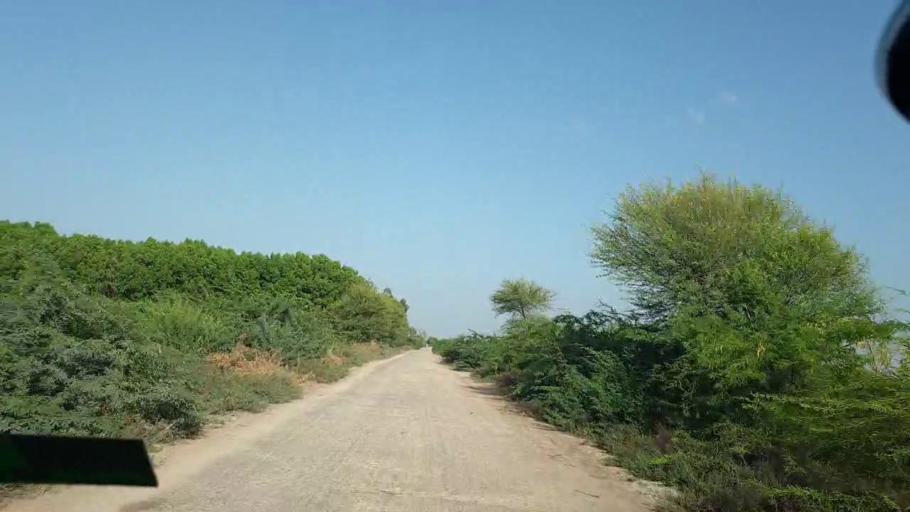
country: PK
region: Sindh
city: Naukot
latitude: 24.7407
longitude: 69.2009
